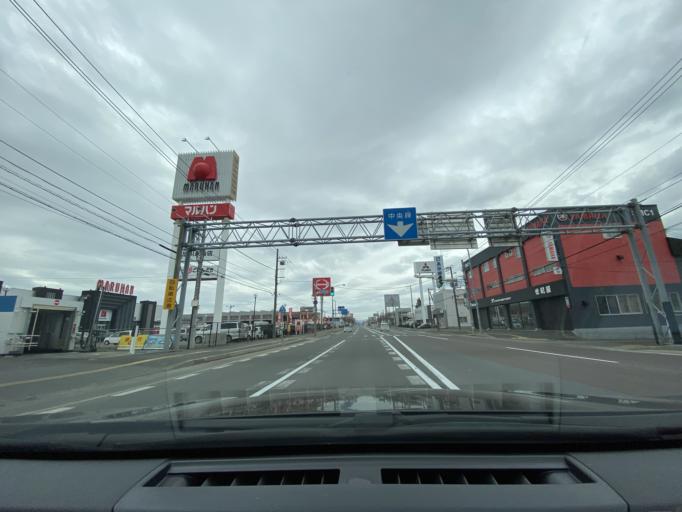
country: JP
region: Hokkaido
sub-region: Asahikawa-shi
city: Asahikawa
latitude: 43.8035
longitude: 142.4226
